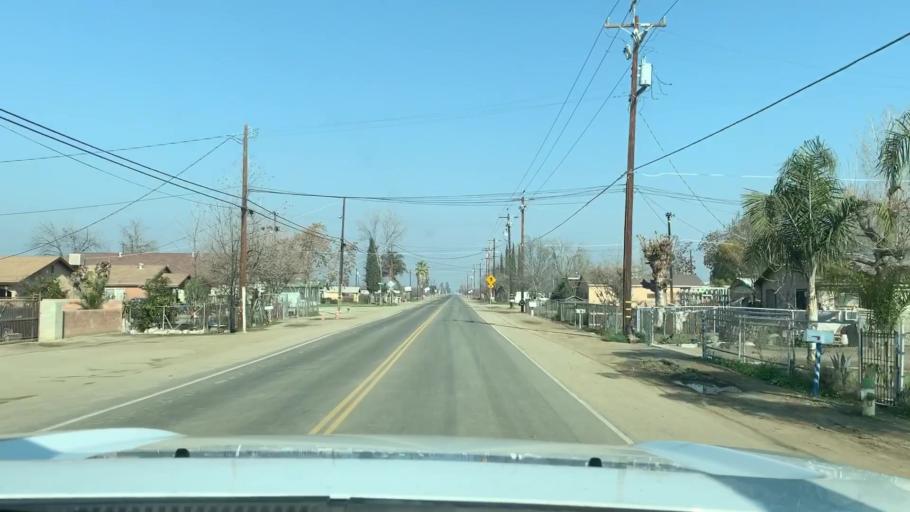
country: US
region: California
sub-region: Kern County
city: Shafter
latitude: 35.4792
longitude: -119.2786
